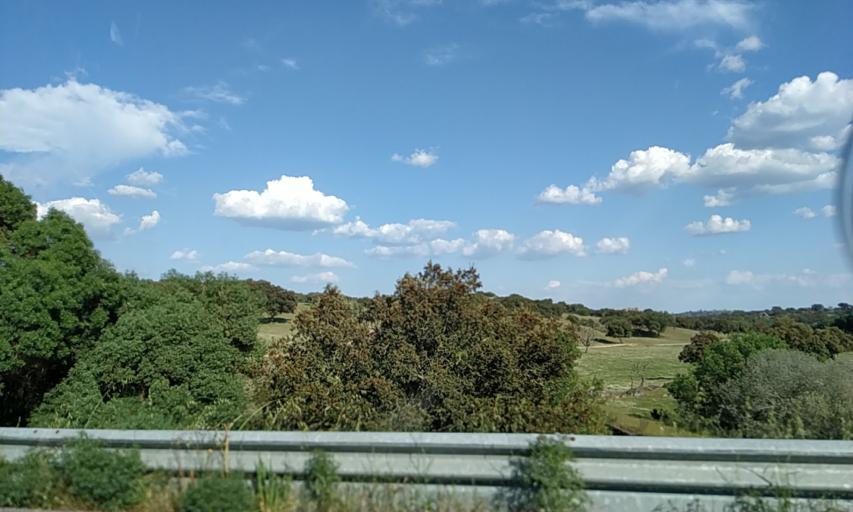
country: PT
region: Portalegre
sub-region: Fronteira
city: Fronteira
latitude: 38.9958
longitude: -7.4715
